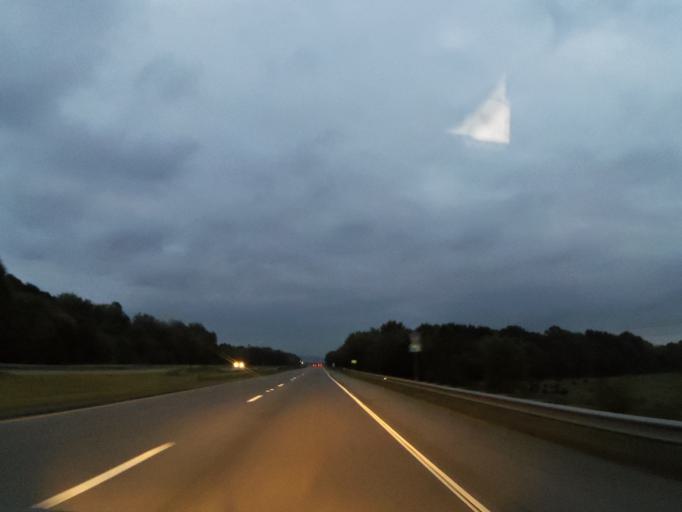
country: US
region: Alabama
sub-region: Madison County
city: New Hope
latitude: 34.6255
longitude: -86.3084
